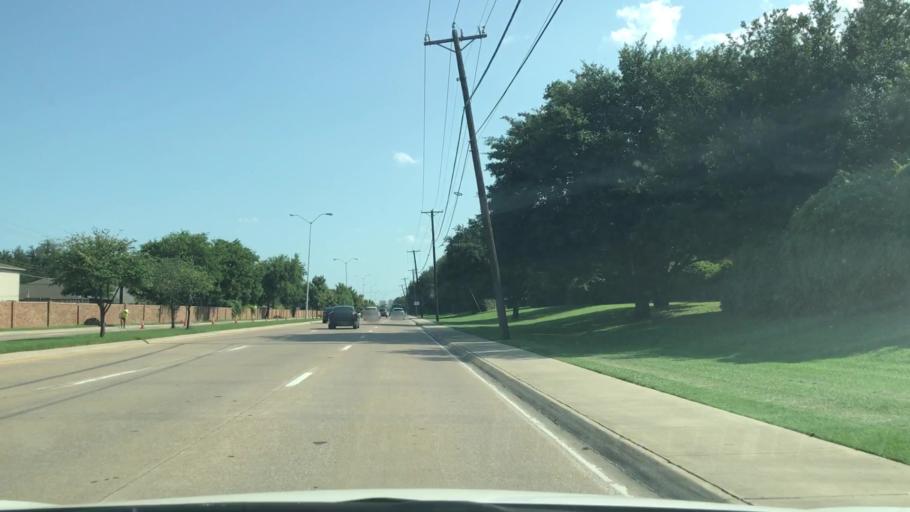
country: US
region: Texas
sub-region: Dallas County
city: Addison
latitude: 32.9807
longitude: -96.8045
